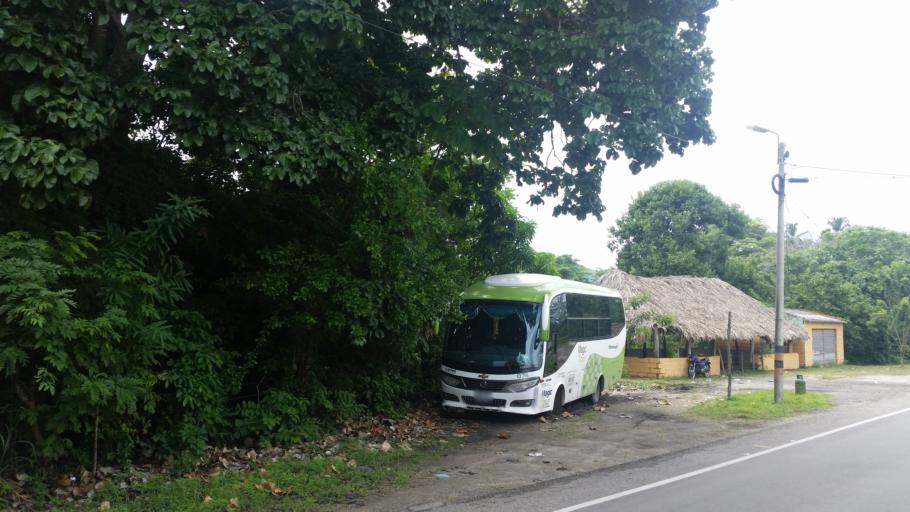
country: CO
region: Magdalena
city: Santa Marta
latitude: 11.2797
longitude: -73.8716
